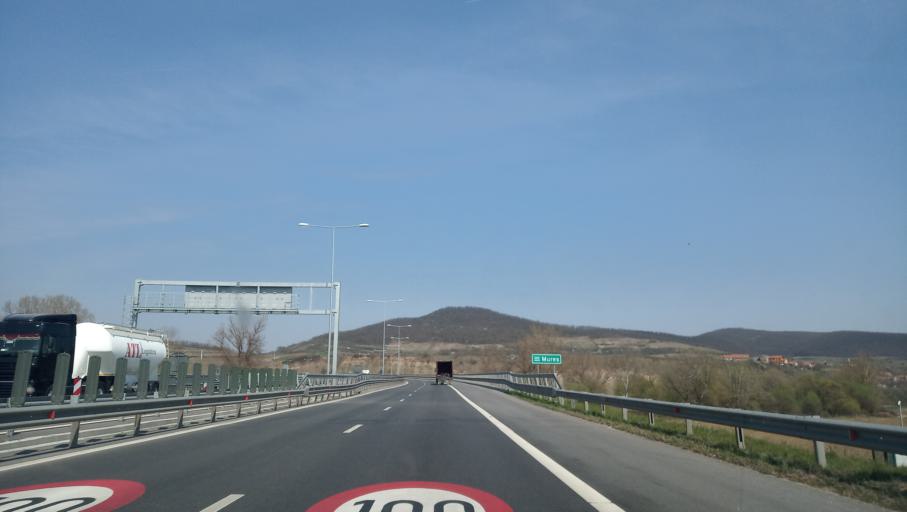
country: RO
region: Alba
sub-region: Municipiul Aiud
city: Aiud
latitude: 46.3354
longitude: 23.7316
